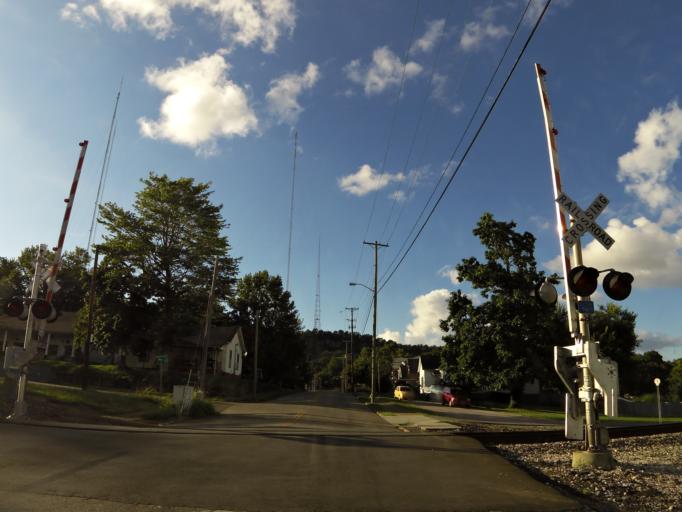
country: US
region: Tennessee
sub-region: Knox County
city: Knoxville
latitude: 35.9978
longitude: -83.9366
